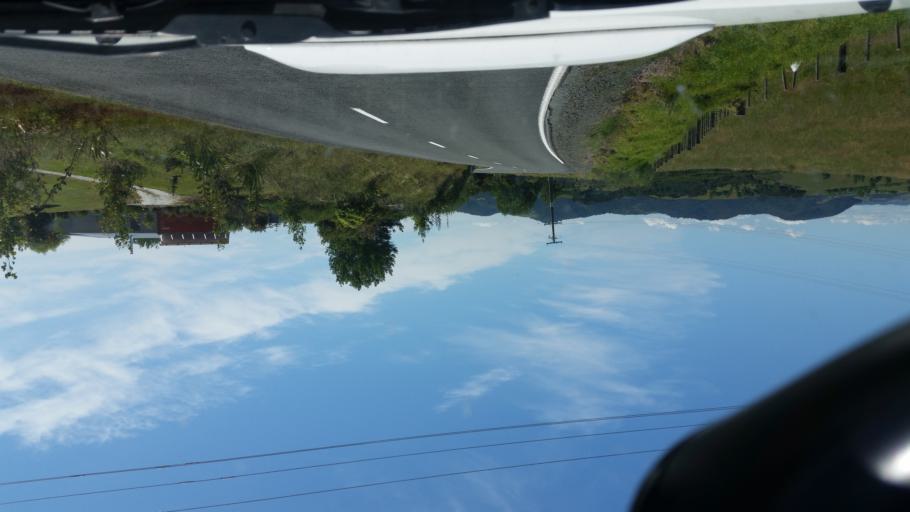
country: NZ
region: Auckland
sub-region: Auckland
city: Wellsford
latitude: -36.1807
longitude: 174.4125
